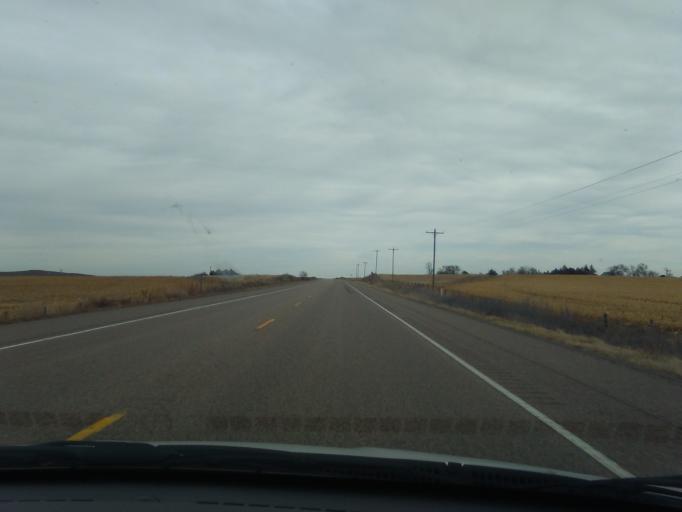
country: US
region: Colorado
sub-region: Yuma County
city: Yuma
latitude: 40.1051
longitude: -102.4820
